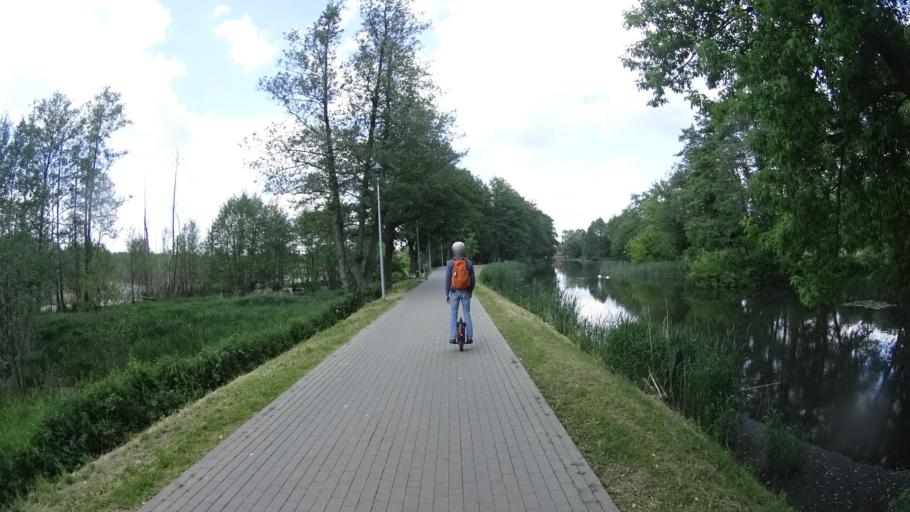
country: PL
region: Masovian Voivodeship
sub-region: Powiat piaseczynski
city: Konstancin-Jeziorna
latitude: 52.0879
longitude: 21.1161
